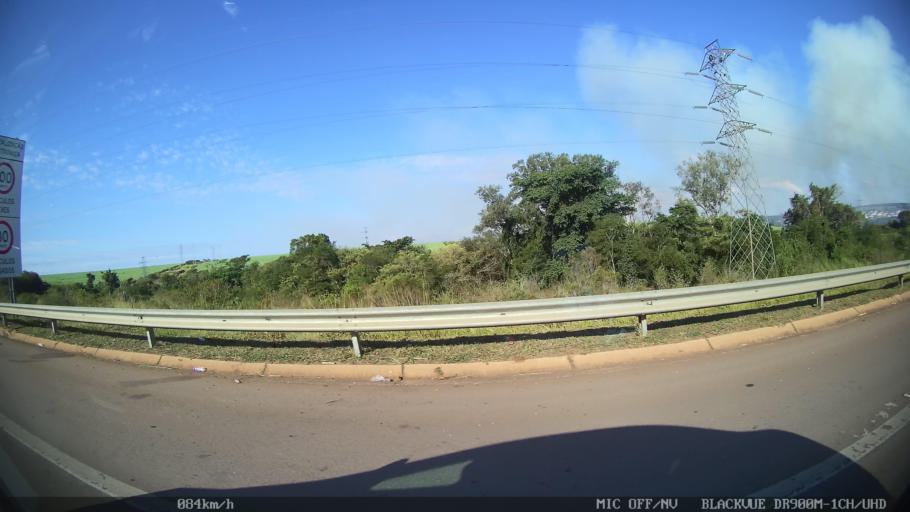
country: BR
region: Sao Paulo
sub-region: Piracicaba
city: Piracicaba
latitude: -22.6882
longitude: -47.5982
